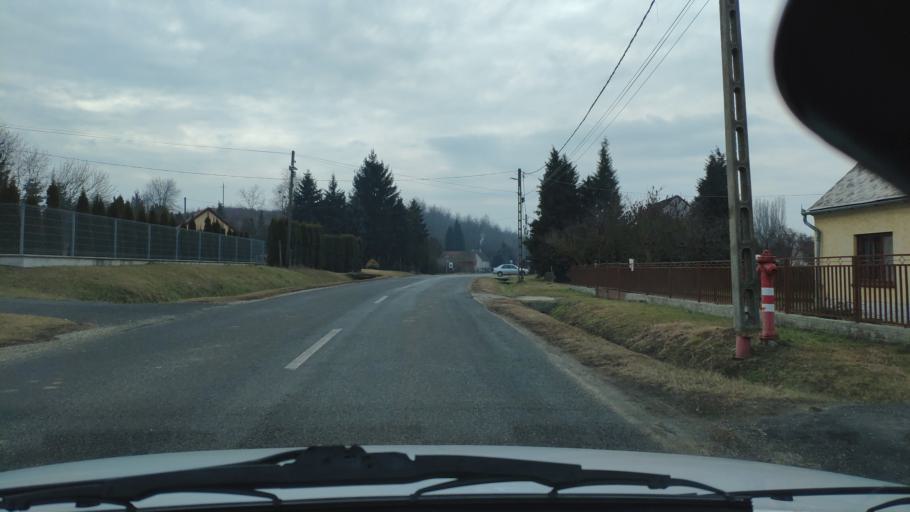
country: HU
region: Zala
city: Nagykanizsa
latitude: 46.5190
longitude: 16.9821
